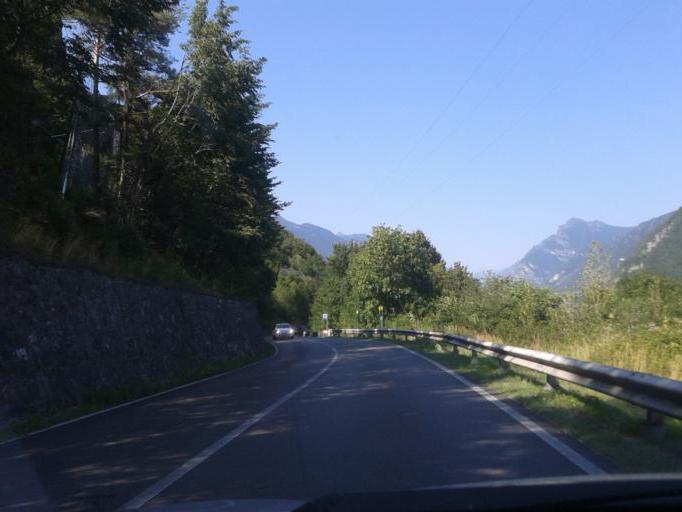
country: IT
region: Lombardy
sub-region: Provincia di Brescia
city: Anfo
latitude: 45.7737
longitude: 10.5023
